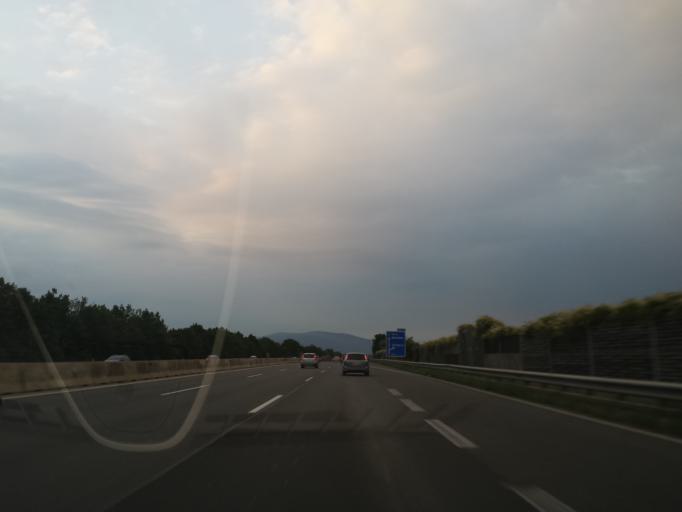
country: AT
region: Lower Austria
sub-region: Politischer Bezirk Baden
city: Leobersdorf
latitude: 47.9394
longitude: 16.2122
